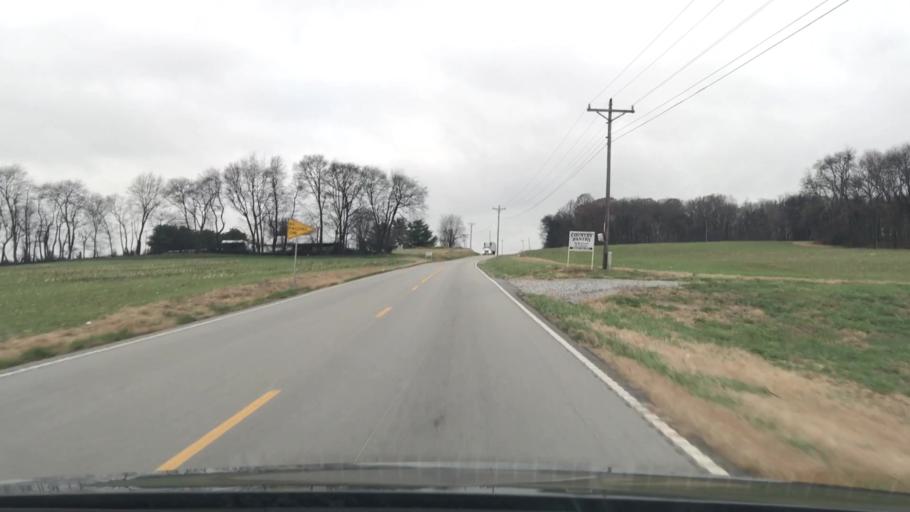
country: US
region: Kentucky
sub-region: Todd County
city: Guthrie
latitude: 36.6827
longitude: -87.2005
